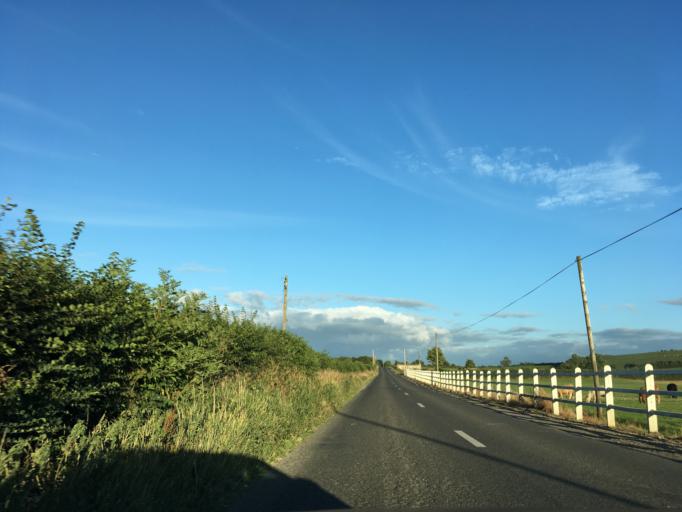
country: IE
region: Munster
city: Cashel
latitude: 52.4871
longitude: -7.9493
